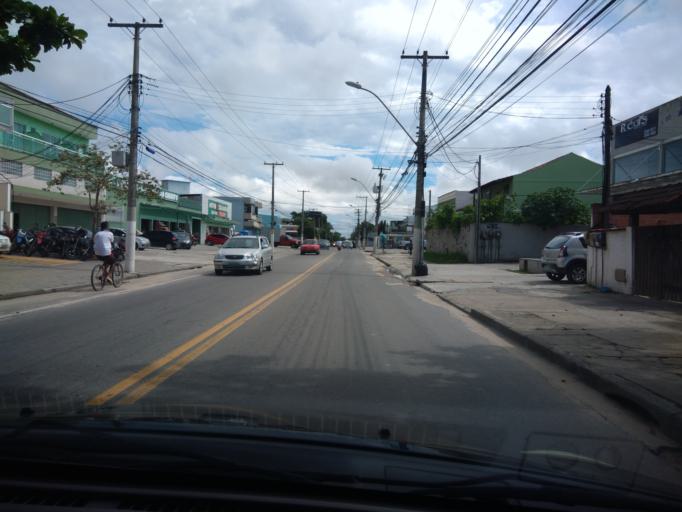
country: BR
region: Rio de Janeiro
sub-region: Niteroi
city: Niteroi
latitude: -22.9374
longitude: -43.0258
